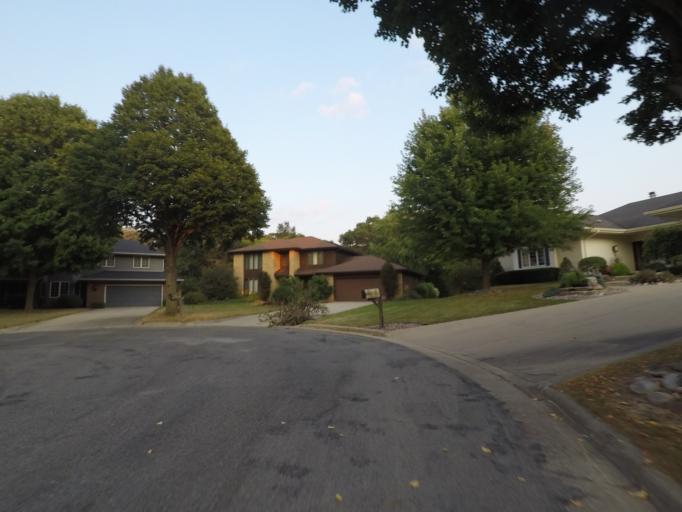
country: US
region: Wisconsin
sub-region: Dane County
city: Middleton
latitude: 43.0692
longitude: -89.5150
